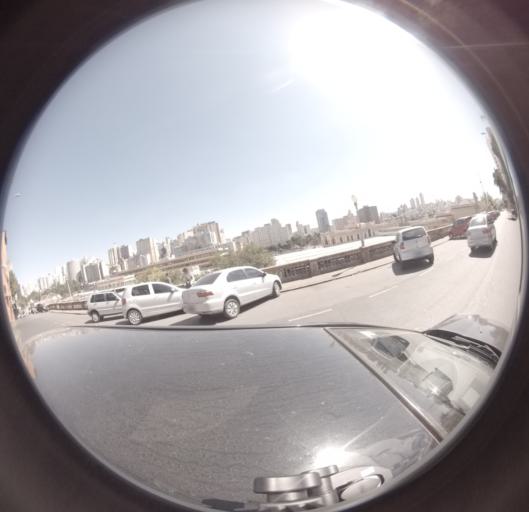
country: BR
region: Minas Gerais
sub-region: Belo Horizonte
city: Belo Horizonte
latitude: -19.9178
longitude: -43.9328
